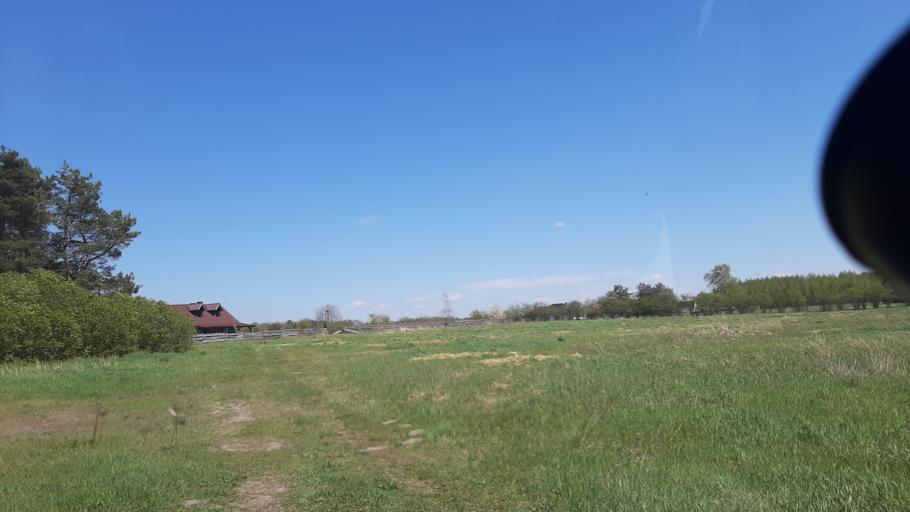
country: PL
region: Lublin Voivodeship
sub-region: Powiat lubelski
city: Garbow
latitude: 51.4021
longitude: 22.3181
